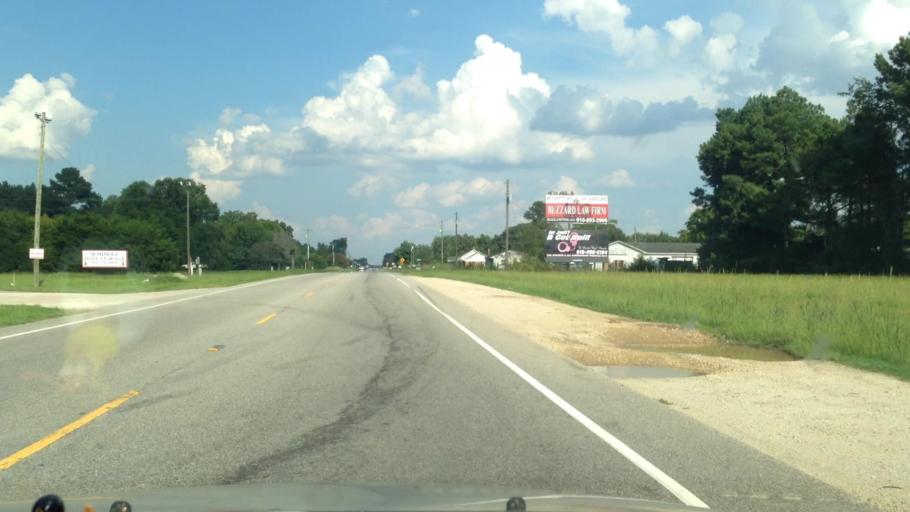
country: US
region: North Carolina
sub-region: Lee County
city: Broadway
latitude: 35.4377
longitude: -79.0312
